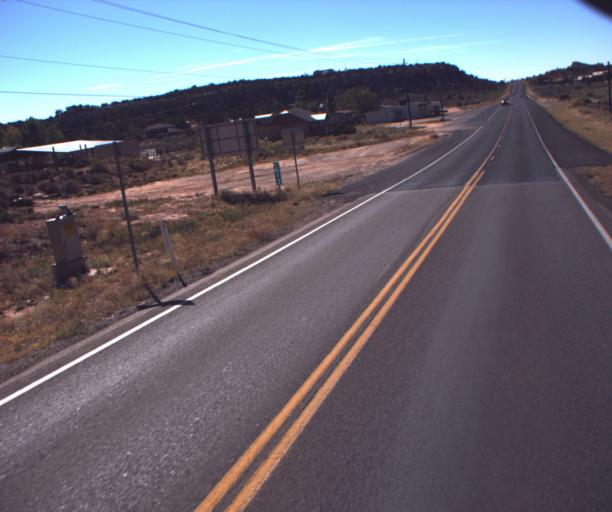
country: US
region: Utah
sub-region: Kane County
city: Kanab
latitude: 37.0010
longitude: -112.5297
